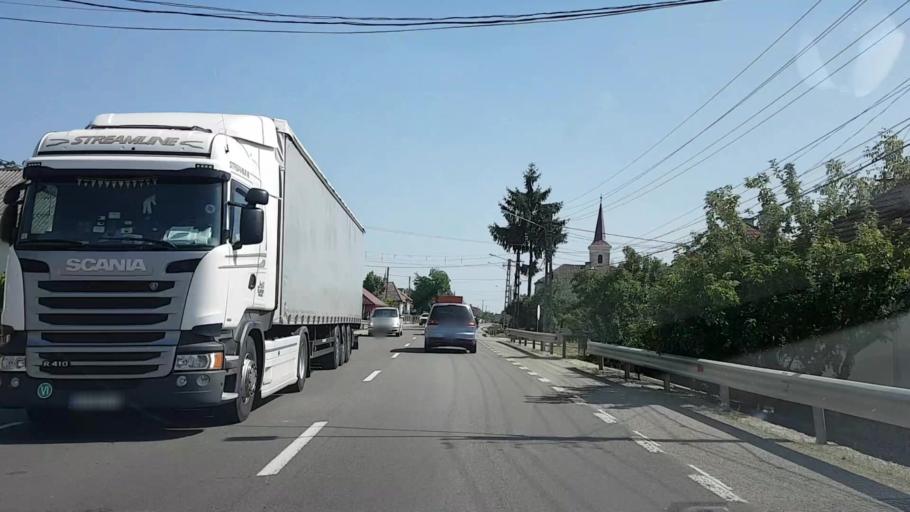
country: RO
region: Bistrita-Nasaud
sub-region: Comuna Sieu-Odorhei
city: Sieu-Odorhei
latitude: 47.1478
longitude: 24.3059
